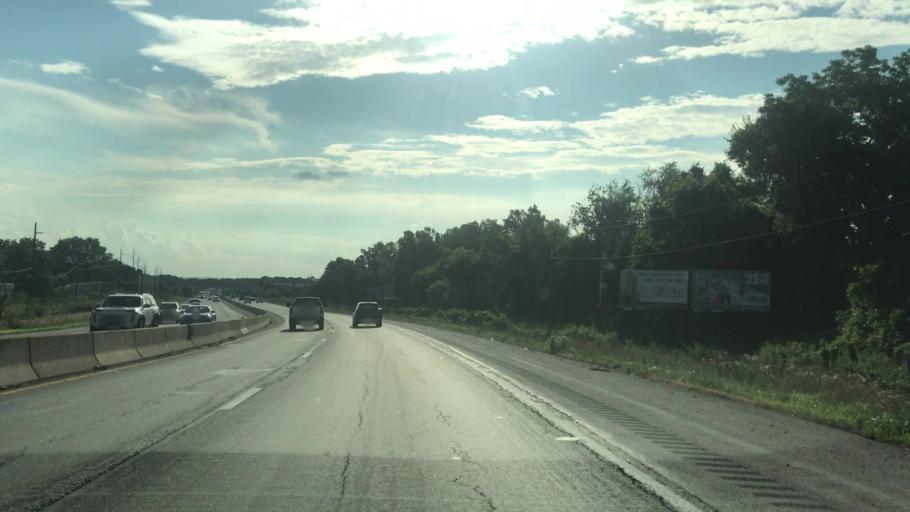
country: US
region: Pennsylvania
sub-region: York County
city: East York
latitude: 39.9798
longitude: -76.7011
